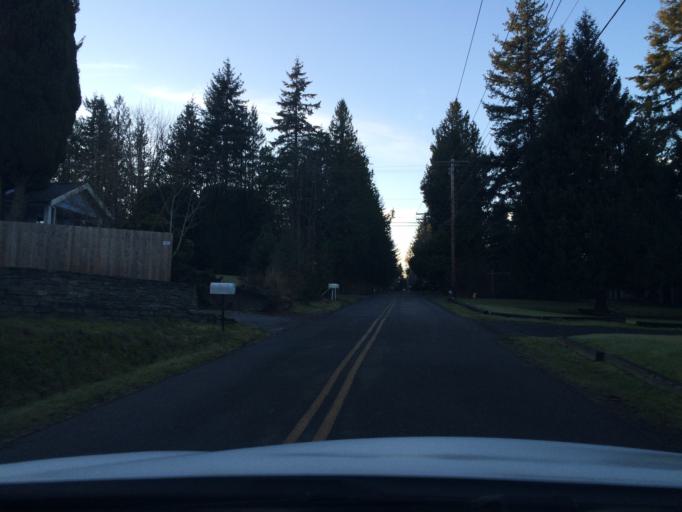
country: US
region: Washington
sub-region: Whatcom County
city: Geneva
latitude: 48.7489
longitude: -122.4007
